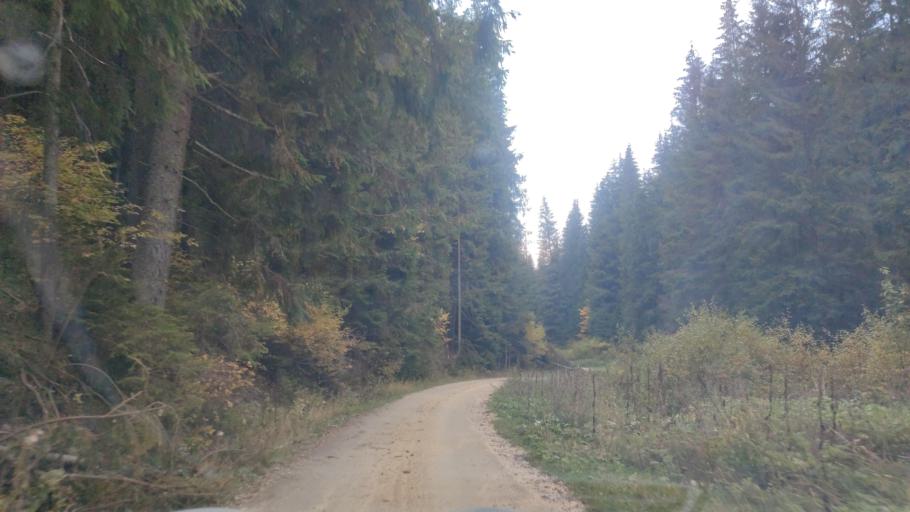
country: RO
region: Harghita
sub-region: Comuna Madaras
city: Madaras
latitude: 46.4733
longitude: 25.6453
